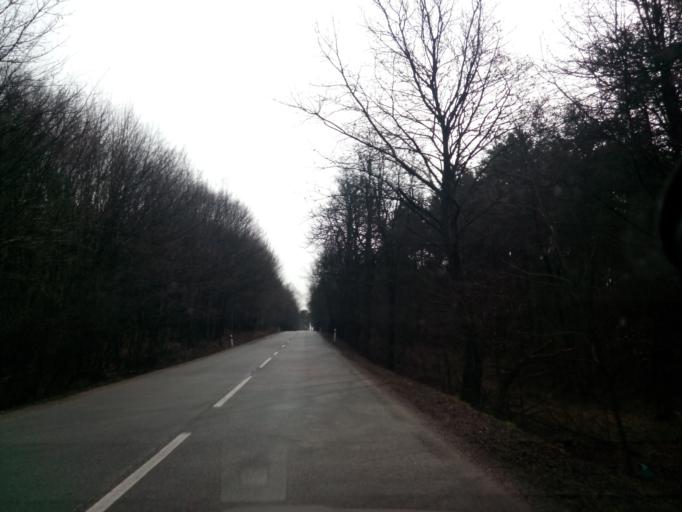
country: SK
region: Kosicky
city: Kosice
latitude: 48.6351
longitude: 21.4481
